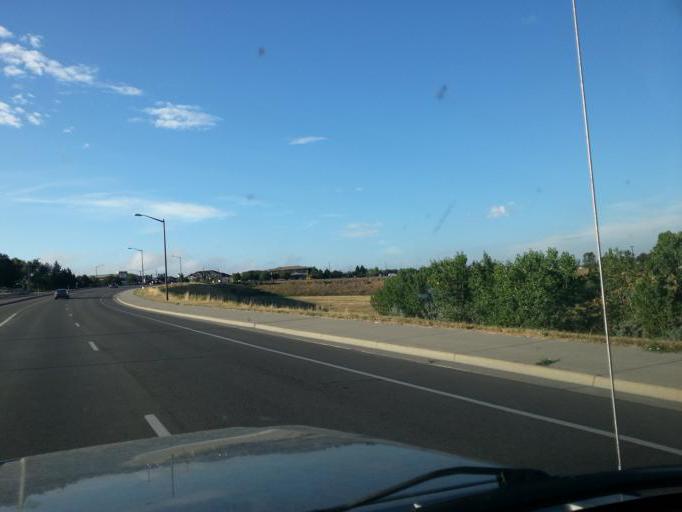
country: US
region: Colorado
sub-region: Larimer County
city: Loveland
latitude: 40.3812
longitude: -105.0962
